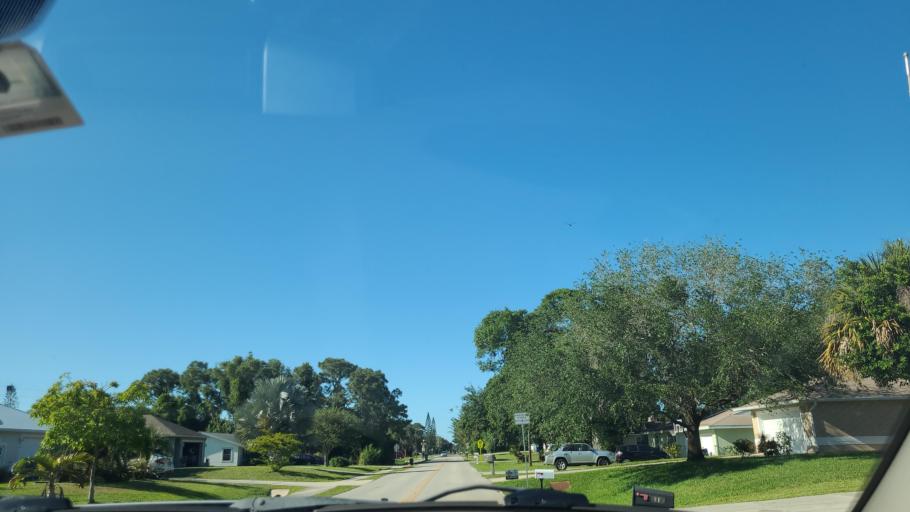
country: US
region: Florida
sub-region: Indian River County
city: Sebastian
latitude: 27.8025
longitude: -80.4808
